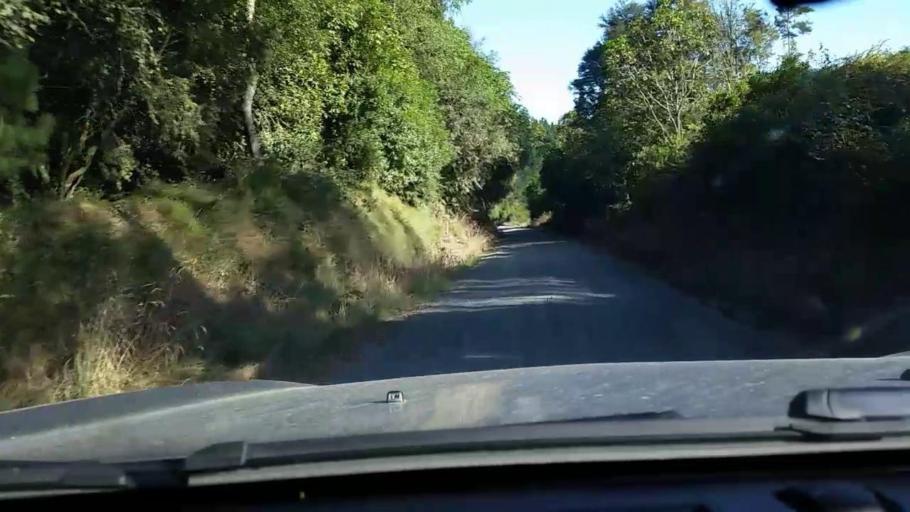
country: NZ
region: Waikato
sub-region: Taupo District
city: Taupo
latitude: -38.4706
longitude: 176.1641
